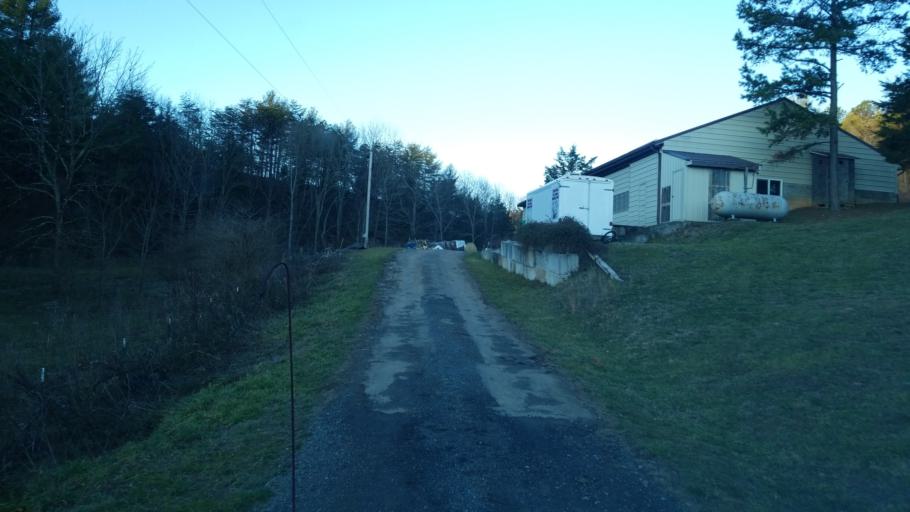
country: US
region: Virginia
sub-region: Giles County
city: Narrows
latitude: 37.1934
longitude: -80.8440
